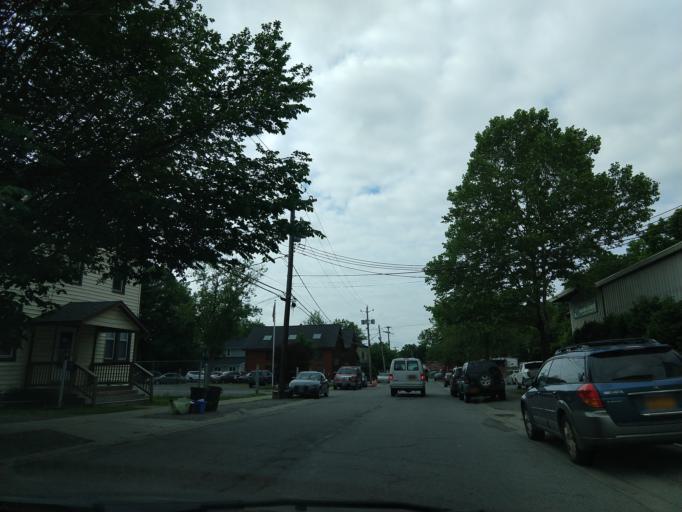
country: US
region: New York
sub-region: Erie County
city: East Aurora
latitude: 42.7667
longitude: -78.6114
